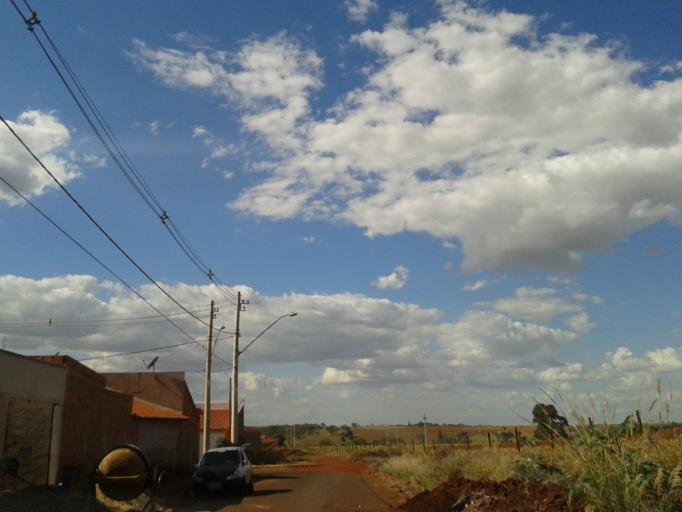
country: BR
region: Minas Gerais
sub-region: Capinopolis
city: Capinopolis
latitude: -18.6980
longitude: -49.5680
